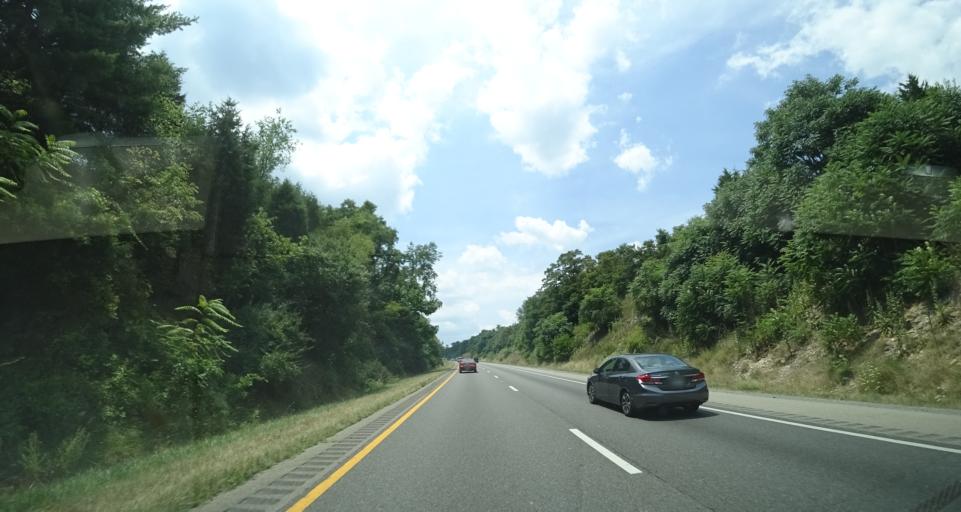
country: US
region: Virginia
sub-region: Pulaski County
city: Dublin
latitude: 37.0882
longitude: -80.6391
